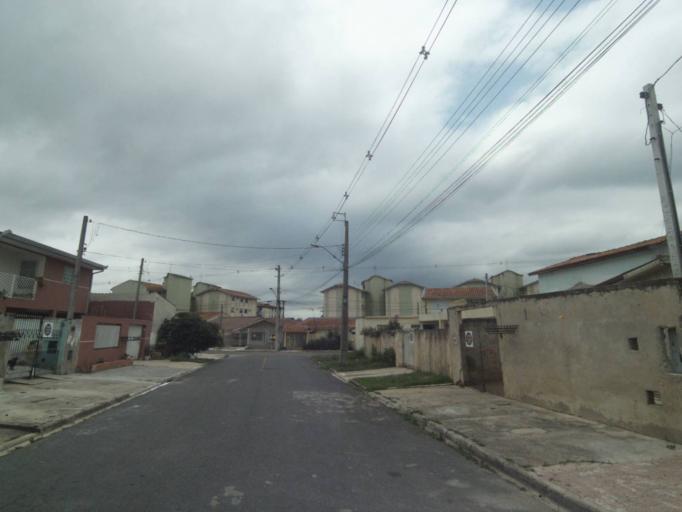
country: BR
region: Parana
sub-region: Sao Jose Dos Pinhais
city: Sao Jose dos Pinhais
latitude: -25.5448
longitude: -49.2514
